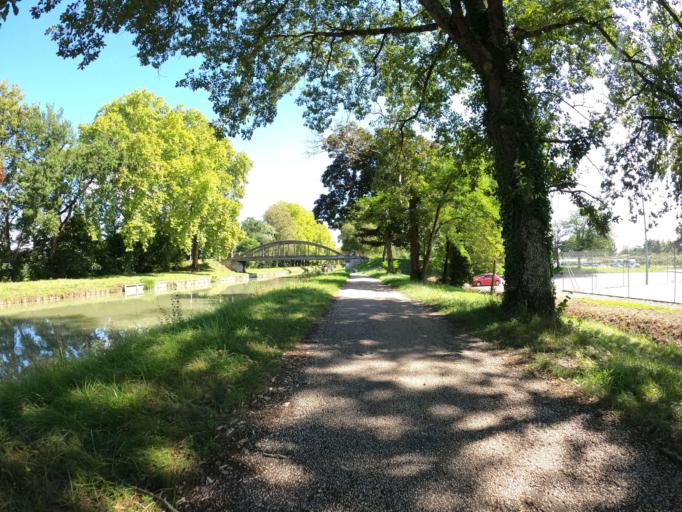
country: FR
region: Midi-Pyrenees
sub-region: Departement du Tarn-et-Garonne
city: Valence
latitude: 44.1158
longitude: 0.8639
